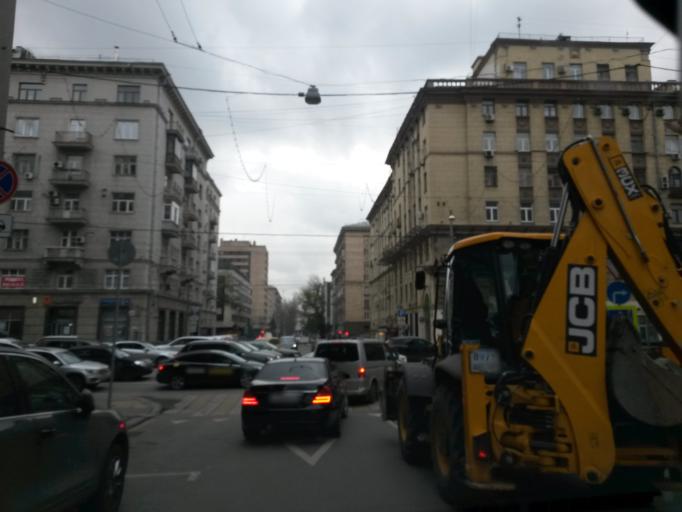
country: RU
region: Moscow
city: Moscow
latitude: 55.7734
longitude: 37.5911
